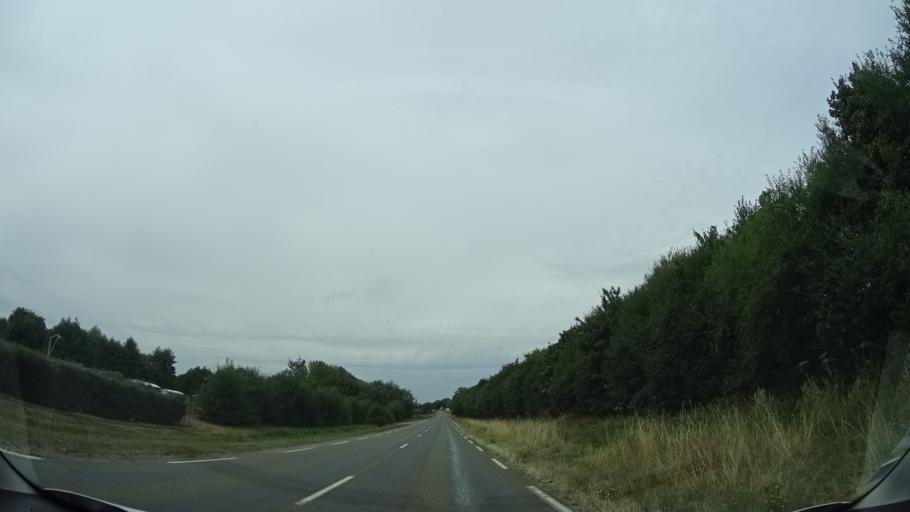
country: FR
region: Pays de la Loire
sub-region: Departement de la Mayenne
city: Meslay-du-Maine
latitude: 47.9473
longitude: -0.5336
